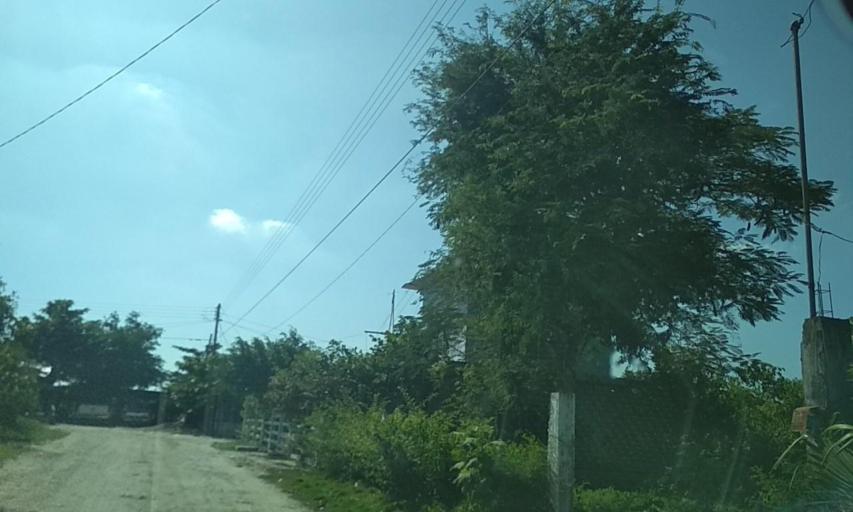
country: MX
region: Veracruz
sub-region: Martinez de la Torre
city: La Union Paso Largo
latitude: 20.1424
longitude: -97.0025
